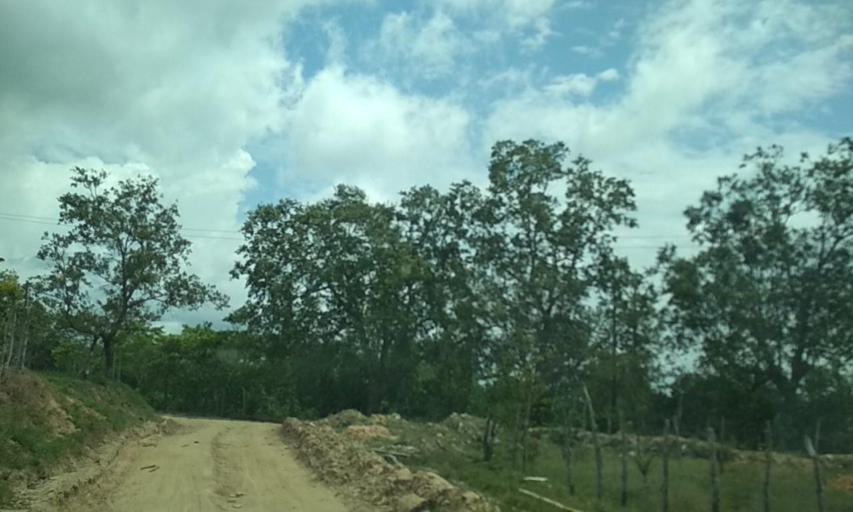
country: MX
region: Veracruz
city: Las Choapas
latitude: 17.8998
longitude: -94.1207
